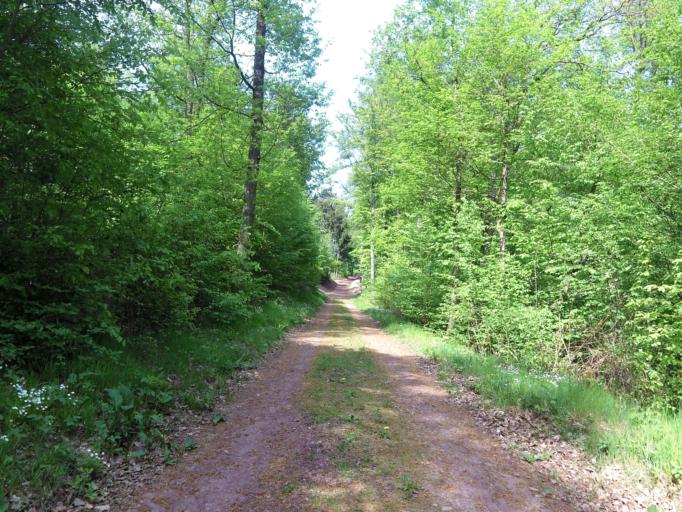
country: DE
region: Thuringia
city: Wolfsburg-Unkeroda
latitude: 50.9438
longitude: 10.2702
